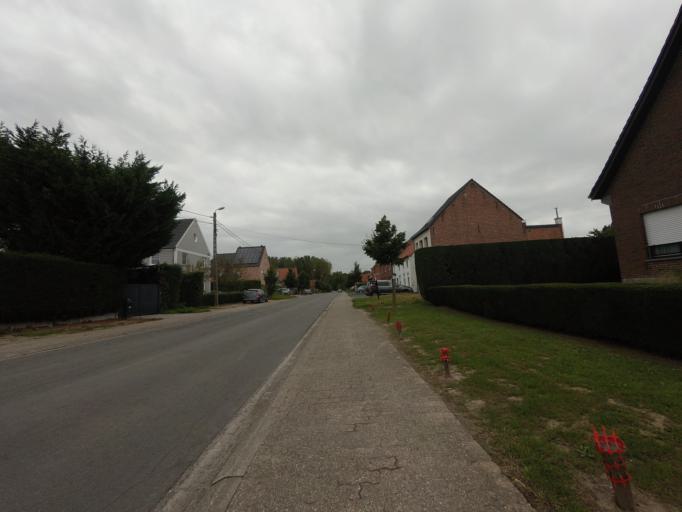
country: BE
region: Flanders
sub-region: Provincie Vlaams-Brabant
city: Meise
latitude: 50.9648
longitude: 4.3203
